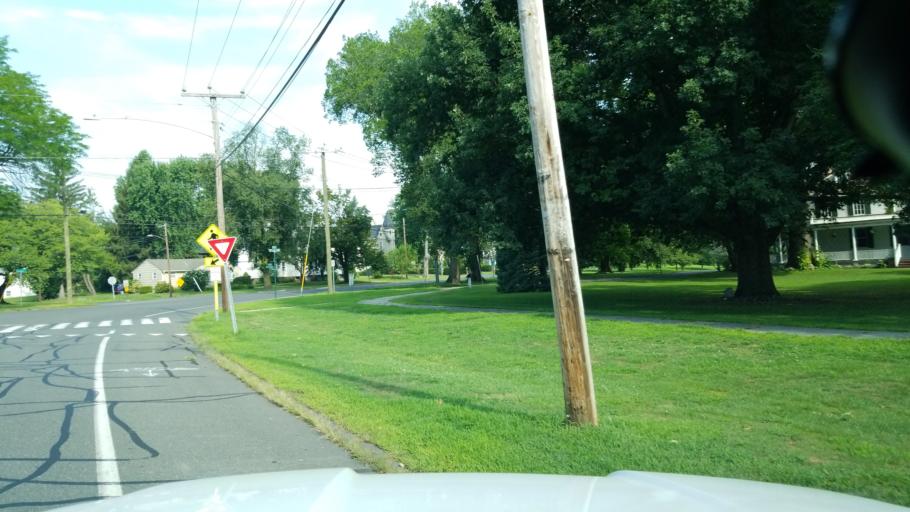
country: US
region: Connecticut
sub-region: Hartford County
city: Wethersfield
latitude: 41.7186
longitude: -72.6595
